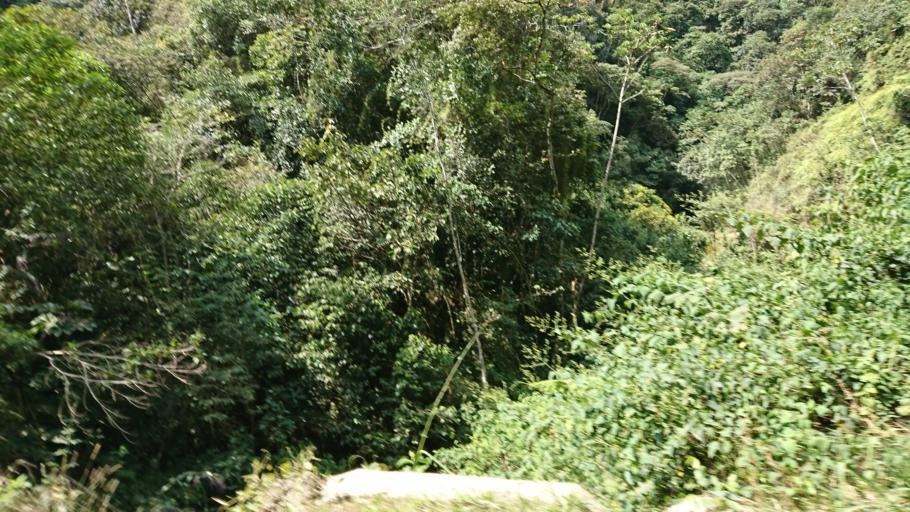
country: BO
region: La Paz
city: Coroico
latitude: -16.1308
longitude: -67.7634
